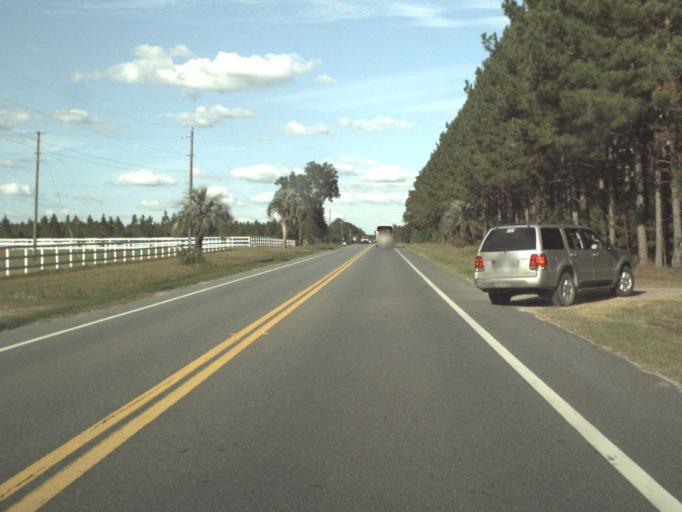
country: US
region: Florida
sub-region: Holmes County
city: Bonifay
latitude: 30.6398
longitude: -85.6899
